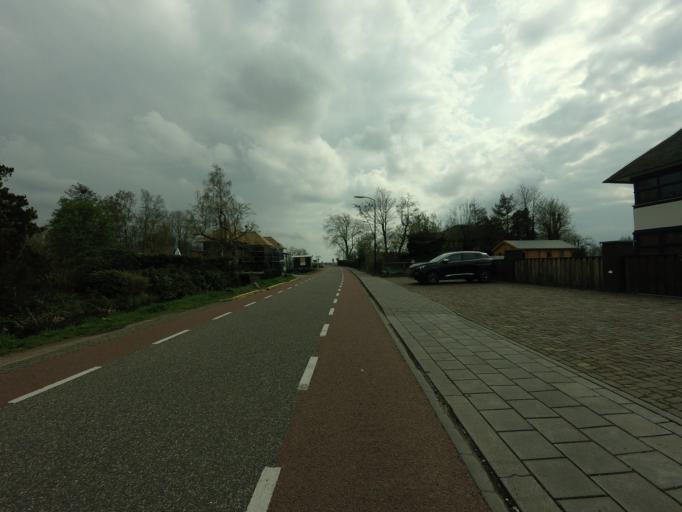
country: NL
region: North Holland
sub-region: Gemeente Wijdemeren
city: Oud-Loosdrecht
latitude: 52.1721
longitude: 5.0699
